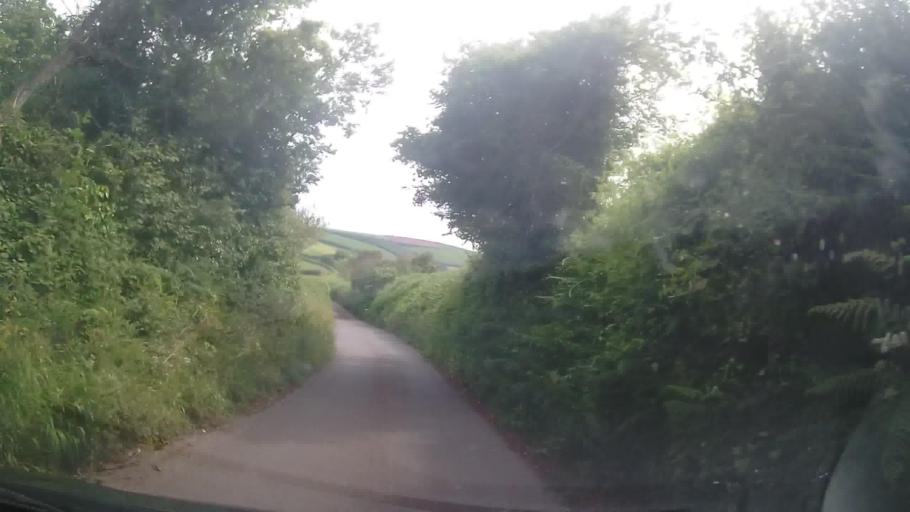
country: GB
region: England
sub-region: Devon
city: Salcombe
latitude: 50.2420
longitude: -3.6792
